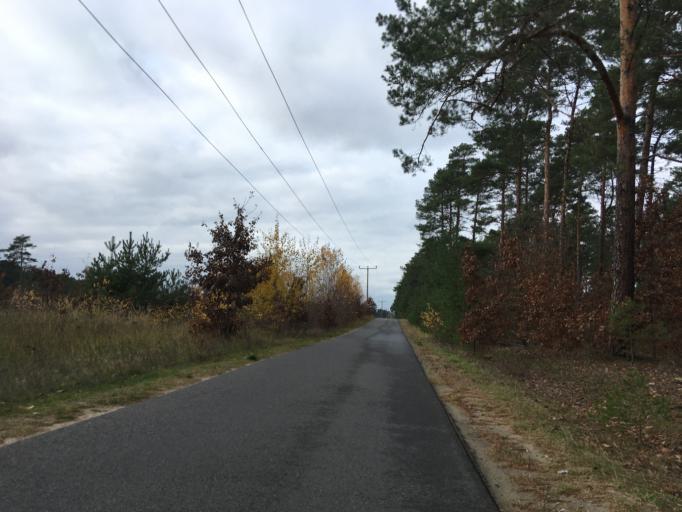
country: DE
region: Brandenburg
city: Jamlitz
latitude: 52.0798
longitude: 14.4548
